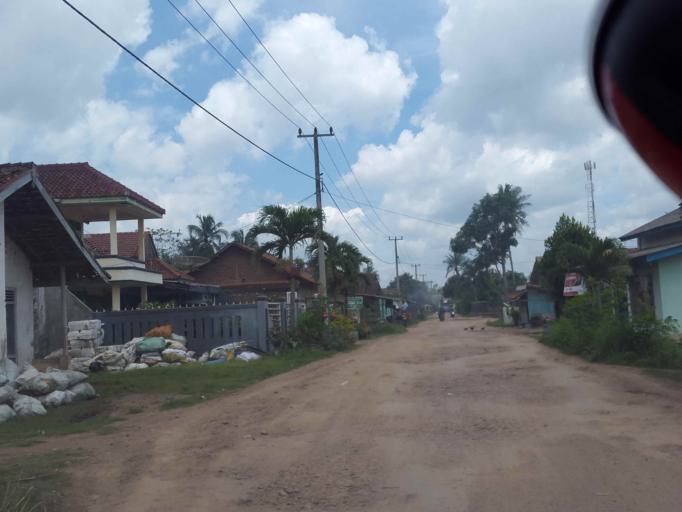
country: ID
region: Lampung
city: Natar
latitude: -5.3123
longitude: 105.2079
